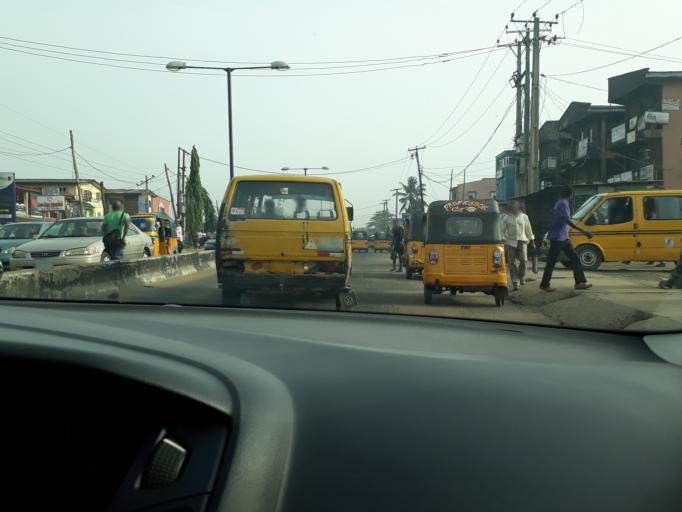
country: NG
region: Lagos
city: Ifako
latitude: 6.6551
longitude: 3.3234
